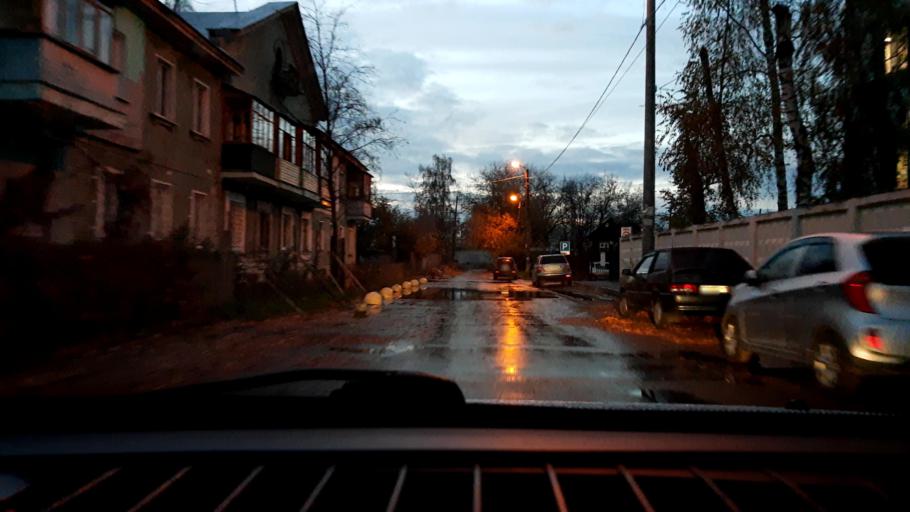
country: RU
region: Nizjnij Novgorod
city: Neklyudovo
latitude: 56.3534
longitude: 43.8510
